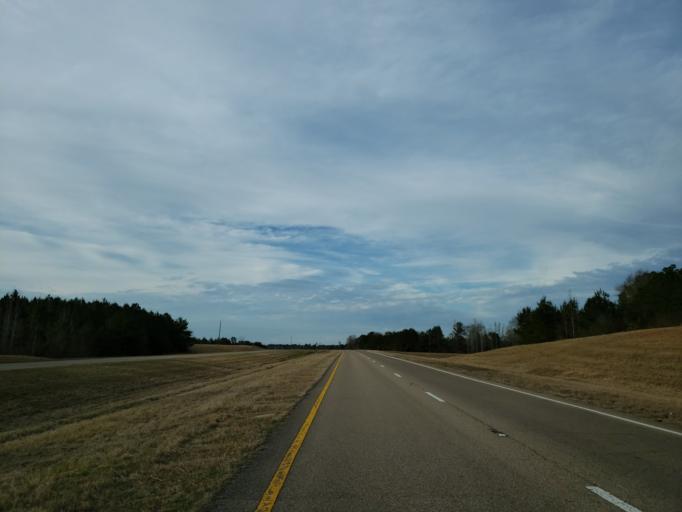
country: US
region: Mississippi
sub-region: Wayne County
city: Waynesboro
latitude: 31.6659
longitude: -88.6044
